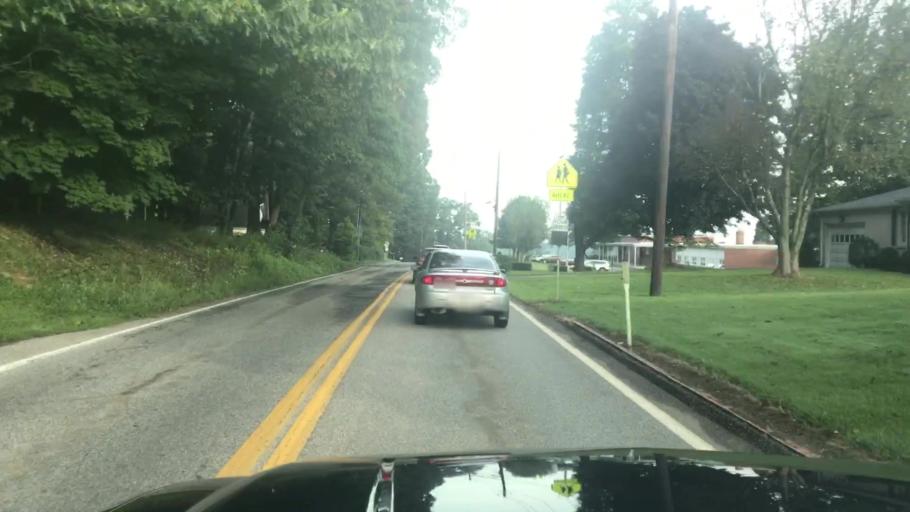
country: US
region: Pennsylvania
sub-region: Cumberland County
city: Shiremanstown
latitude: 40.2011
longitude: -76.9514
